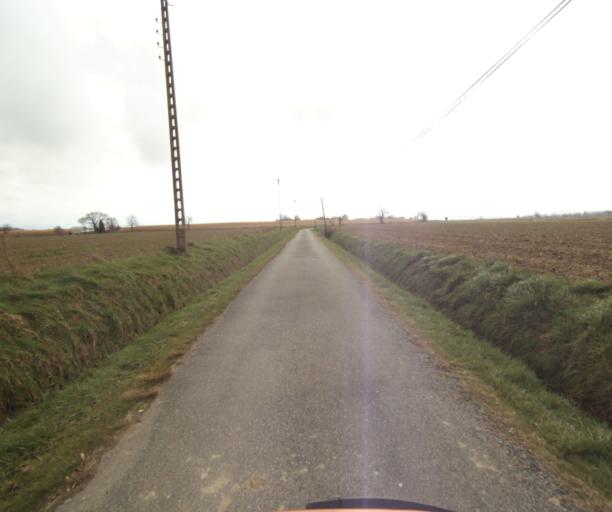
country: FR
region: Midi-Pyrenees
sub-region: Departement de l'Ariege
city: Mazeres
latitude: 43.1898
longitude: 1.6631
